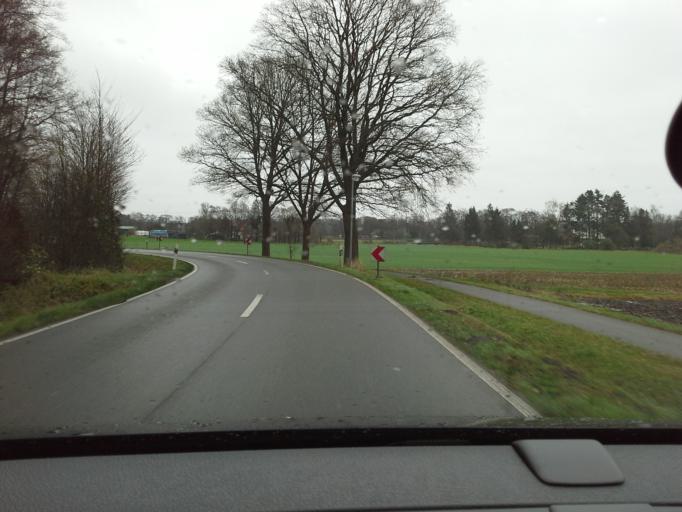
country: DE
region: Schleswig-Holstein
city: Bilsen
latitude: 53.7481
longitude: 9.8813
